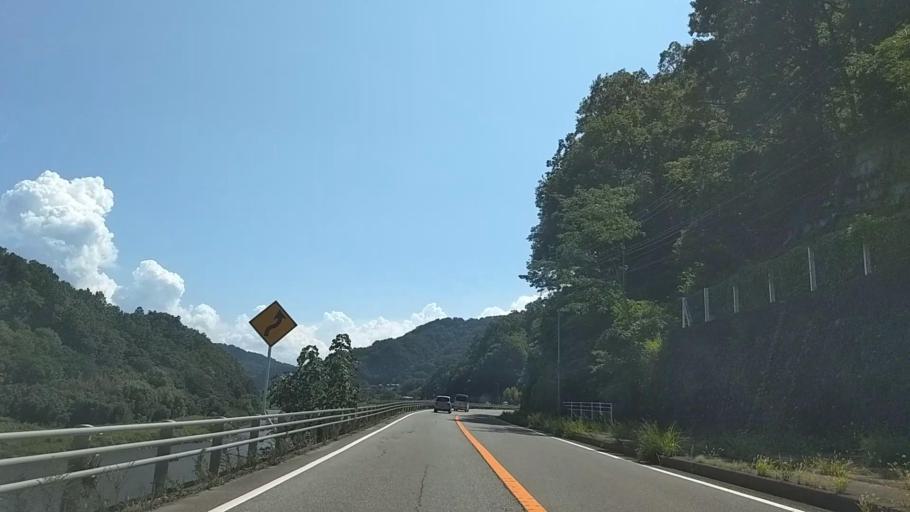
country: JP
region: Yamanashi
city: Ryuo
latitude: 35.5318
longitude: 138.4506
